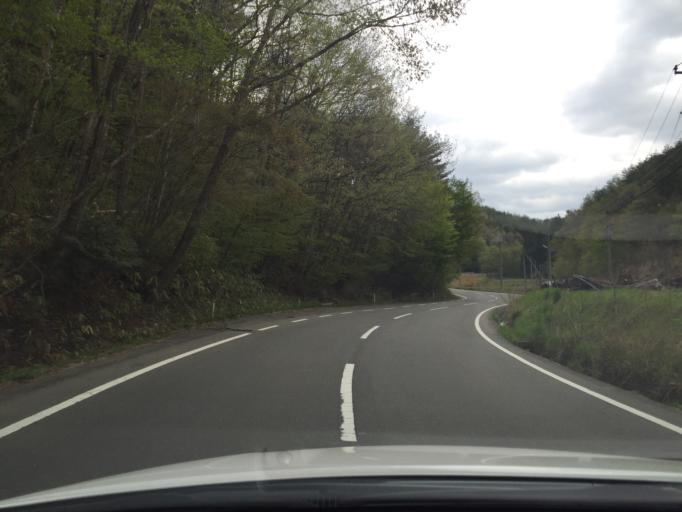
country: JP
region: Fukushima
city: Yanagawamachi-saiwaicho
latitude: 37.7205
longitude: 140.7321
